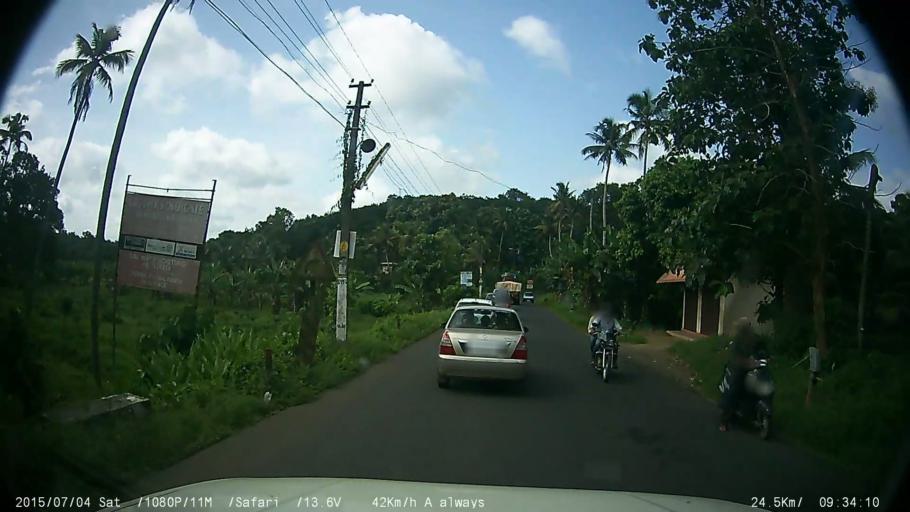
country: IN
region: Kerala
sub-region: Kottayam
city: Kottayam
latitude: 9.6147
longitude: 76.6045
